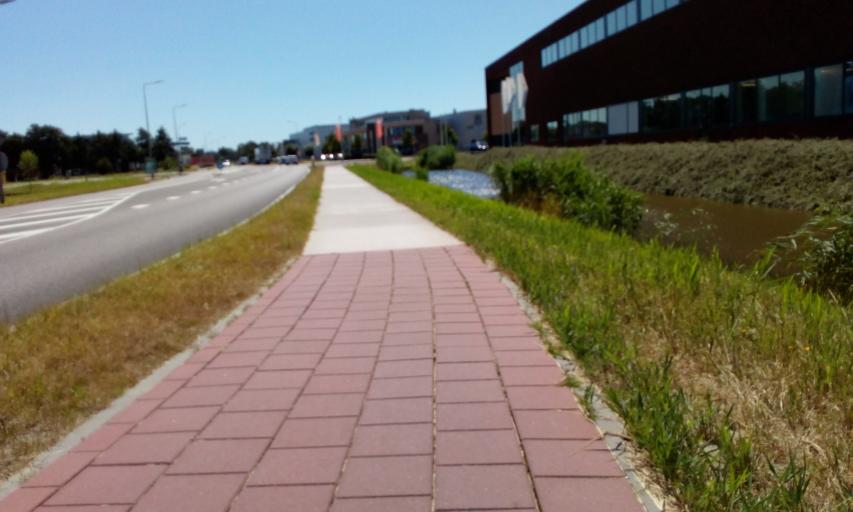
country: NL
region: South Holland
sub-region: Gemeente Teylingen
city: Voorhout
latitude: 52.2135
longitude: 4.4940
